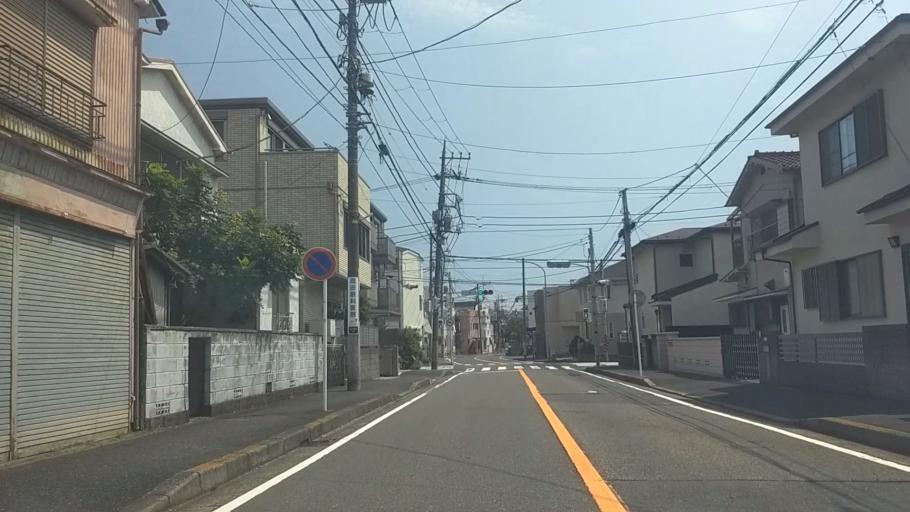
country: JP
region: Kanagawa
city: Yokohama
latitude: 35.4901
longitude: 139.6425
